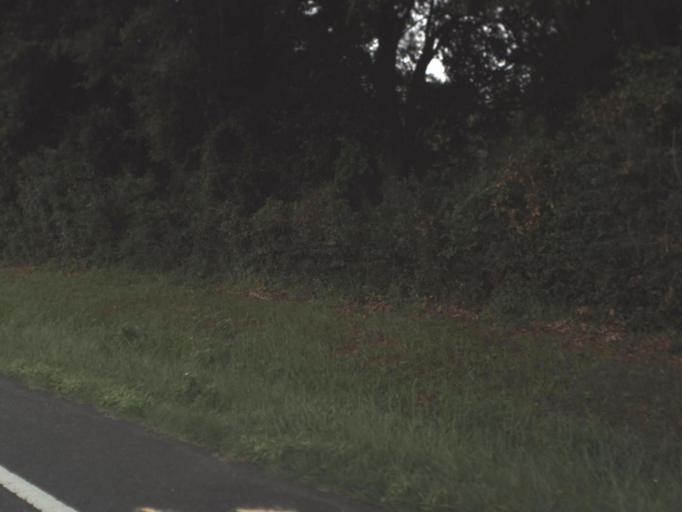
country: US
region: Florida
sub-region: Levy County
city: Williston
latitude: 29.2651
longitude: -82.4417
